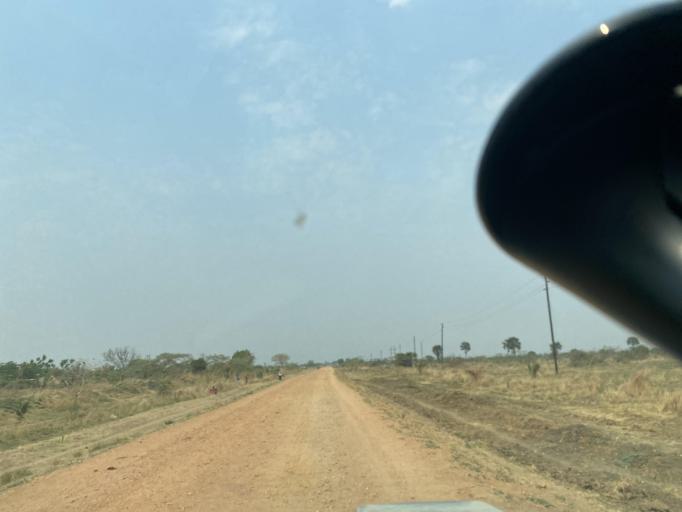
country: ZM
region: Lusaka
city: Kafue
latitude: -15.6756
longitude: 28.0155
